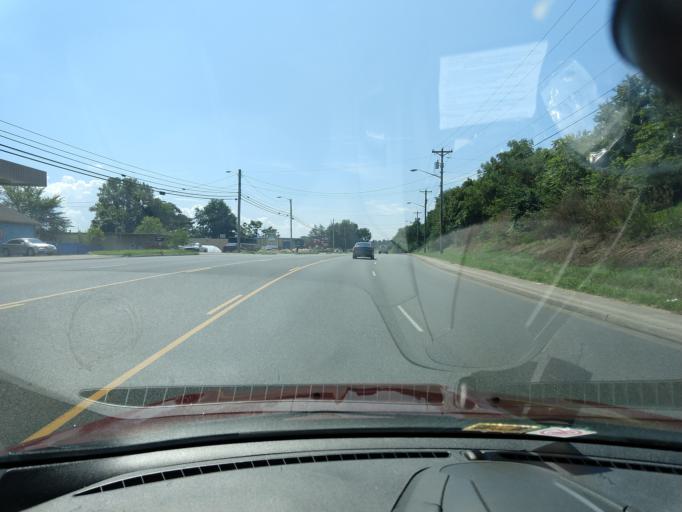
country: US
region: Virginia
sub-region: City of Harrisonburg
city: Harrisonburg
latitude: 38.4671
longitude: -78.8706
